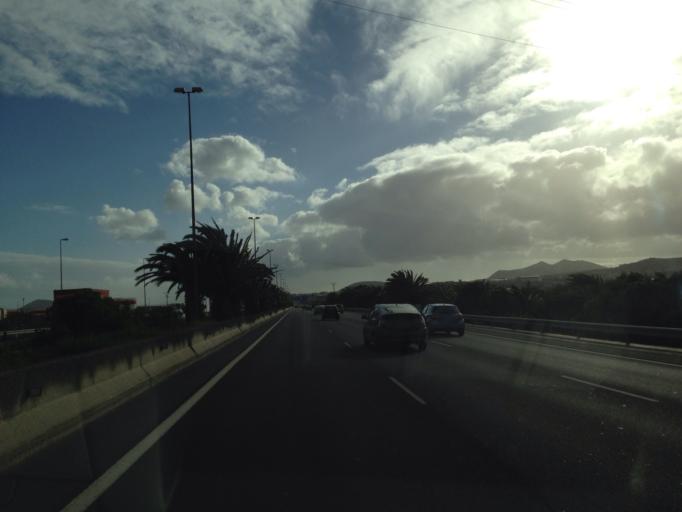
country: ES
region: Canary Islands
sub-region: Provincia de Las Palmas
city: Ingenio
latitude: 27.9360
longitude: -15.3928
